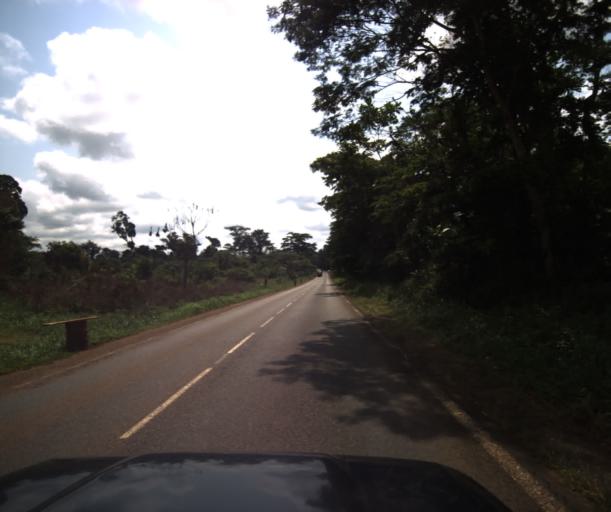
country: CM
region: Centre
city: Eseka
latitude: 3.8914
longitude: 10.7810
